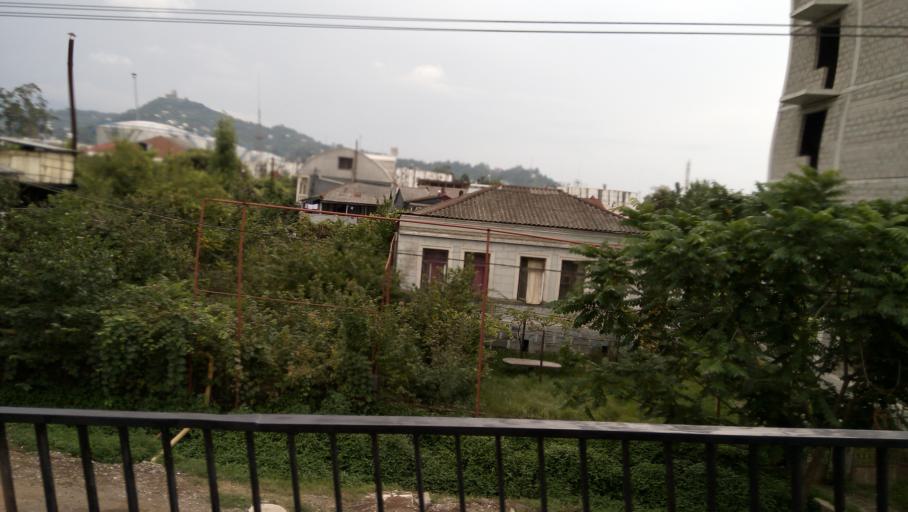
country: GE
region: Ajaria
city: Batumi
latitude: 41.6469
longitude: 41.6681
